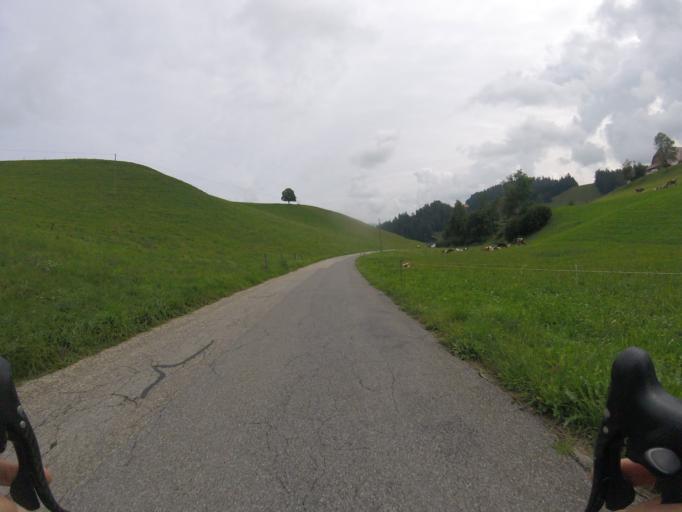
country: CH
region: Bern
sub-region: Emmental District
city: Lutzelfluh
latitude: 46.9773
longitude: 7.6848
